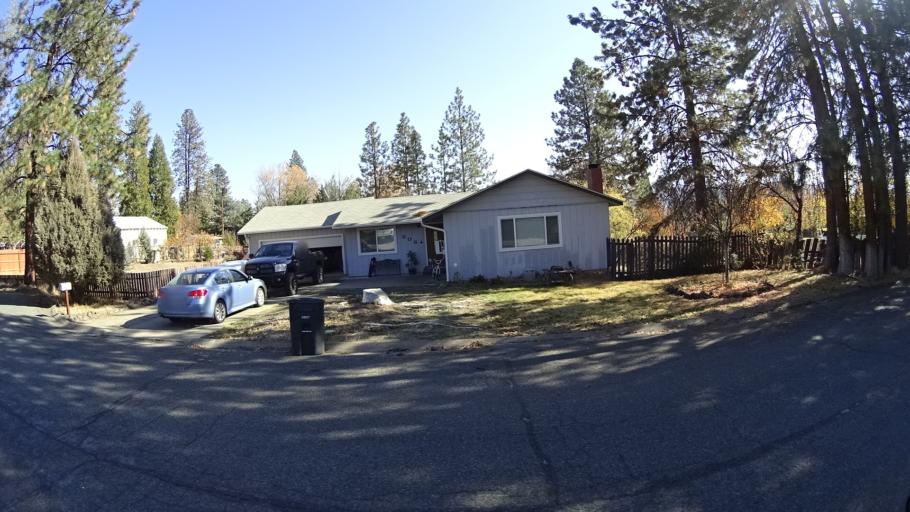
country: US
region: California
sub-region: Siskiyou County
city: Yreka
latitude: 41.7390
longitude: -122.6500
